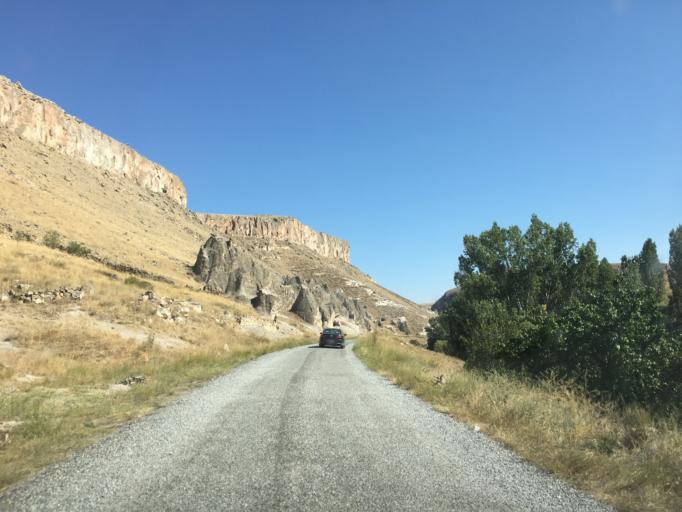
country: TR
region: Kayseri
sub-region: Yesilhisar
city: Yesilhisar
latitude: 38.3505
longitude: 34.9672
